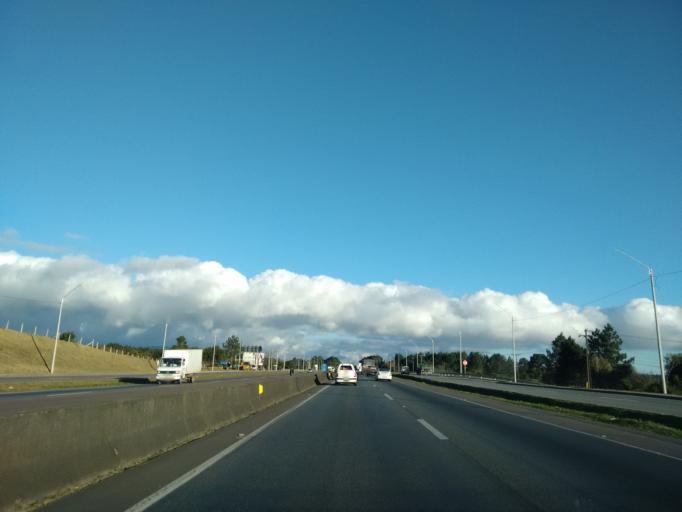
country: BR
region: Parana
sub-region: Sao Jose Dos Pinhais
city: Sao Jose dos Pinhais
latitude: -25.6760
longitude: -49.1503
